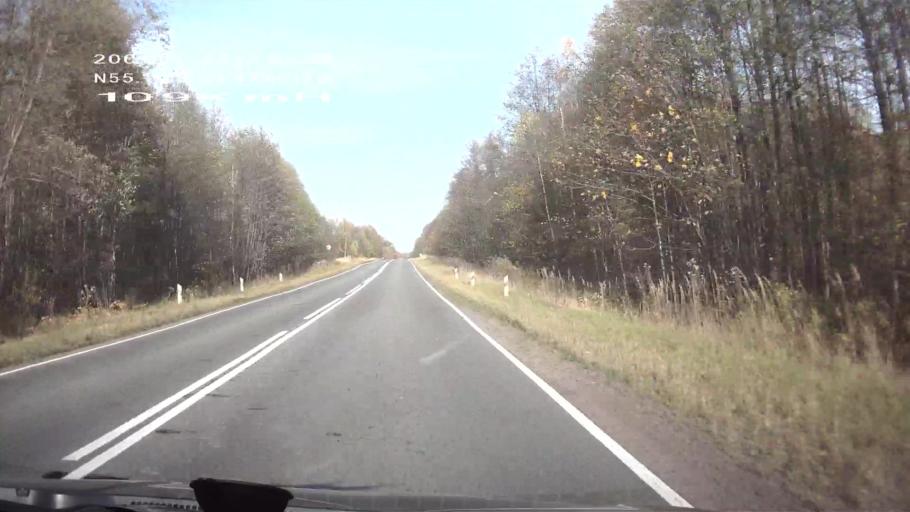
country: RU
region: Chuvashia
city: Buinsk
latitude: 55.1769
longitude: 47.0612
